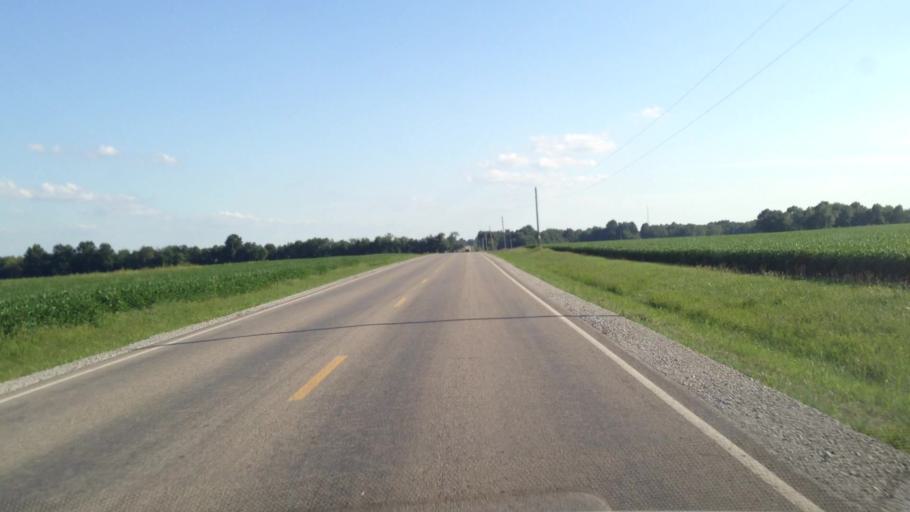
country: US
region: Kansas
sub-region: Crawford County
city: Pittsburg
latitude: 37.3584
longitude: -94.6315
